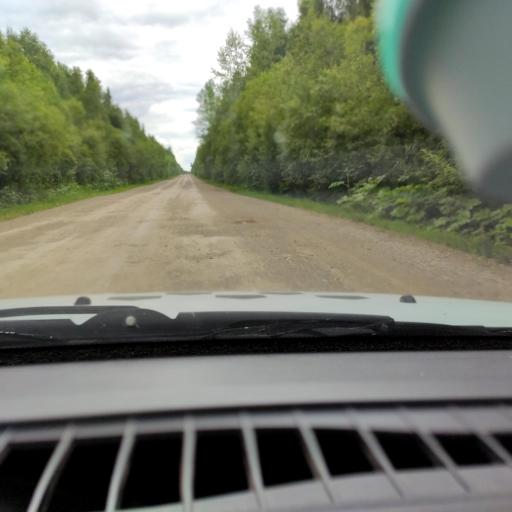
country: RU
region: Perm
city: Suksun
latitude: 57.1584
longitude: 57.5355
